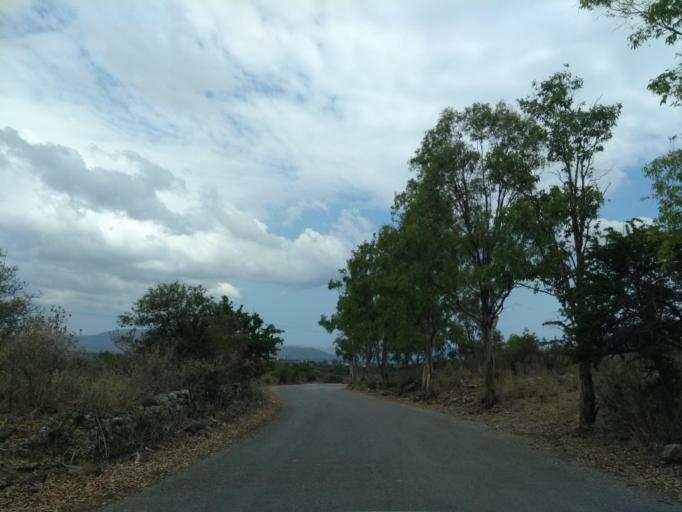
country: GR
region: Crete
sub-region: Nomos Chanias
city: Kalivai
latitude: 35.4071
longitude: 24.2141
